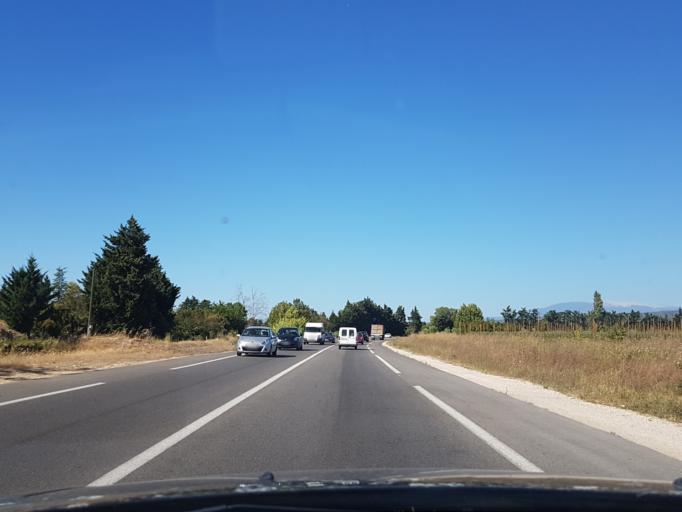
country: FR
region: Provence-Alpes-Cote d'Azur
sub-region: Departement du Vaucluse
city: L'Isle-sur-la-Sorgue
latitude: 43.8909
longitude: 5.0426
